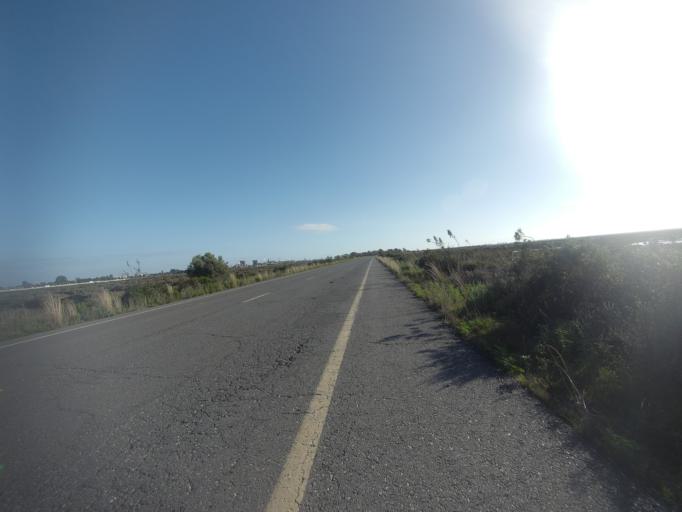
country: ES
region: Andalusia
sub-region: Provincia de Huelva
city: Huelva
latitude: 37.2464
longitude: -6.9667
